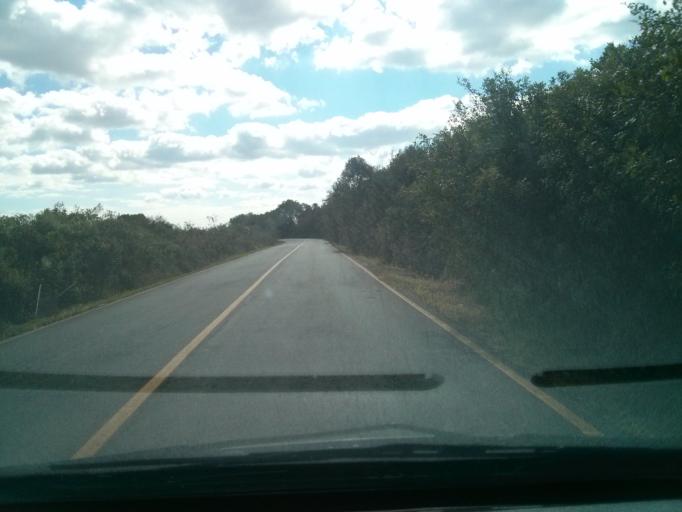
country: BR
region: Parana
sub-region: Sao Jose Dos Pinhais
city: Sao Jose dos Pinhais
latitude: -25.5358
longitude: -49.2259
